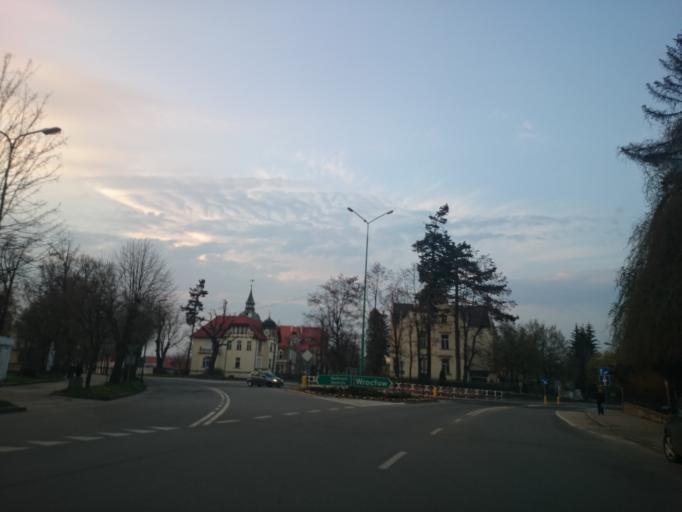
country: PL
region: Lower Silesian Voivodeship
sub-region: Powiat zabkowicki
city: Zabkowice Slaskie
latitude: 50.5939
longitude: 16.8126
